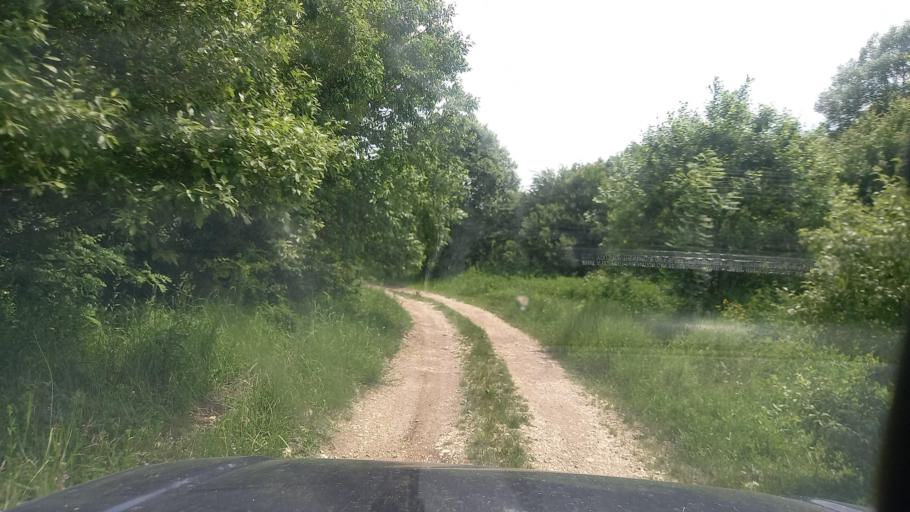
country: RU
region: Karachayevo-Cherkesiya
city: Pregradnaya
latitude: 44.0894
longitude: 41.1545
